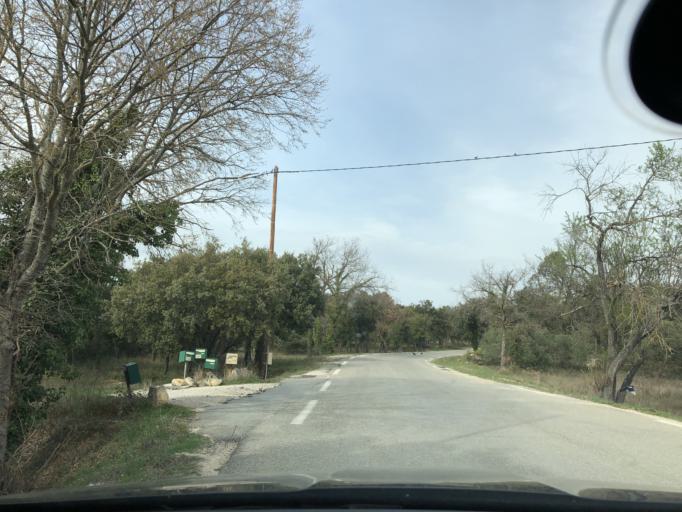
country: FR
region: Provence-Alpes-Cote d'Azur
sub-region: Departement du Vaucluse
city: Menerbes
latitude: 43.8411
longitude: 5.2166
